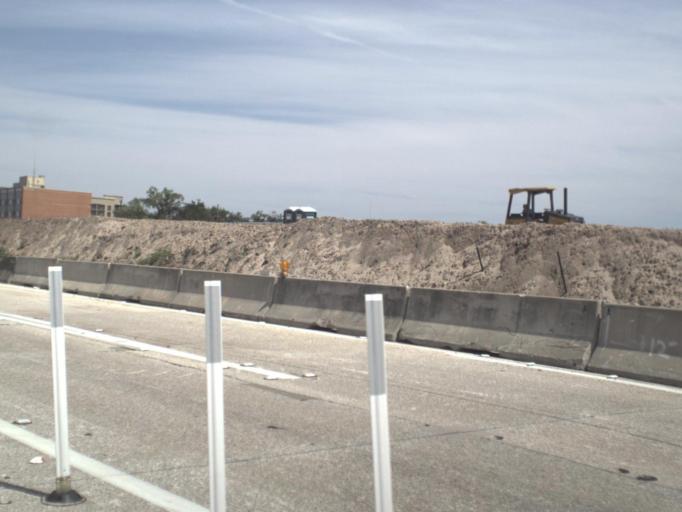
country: US
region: Florida
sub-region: Duval County
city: Jacksonville
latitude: 30.3138
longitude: -81.6577
